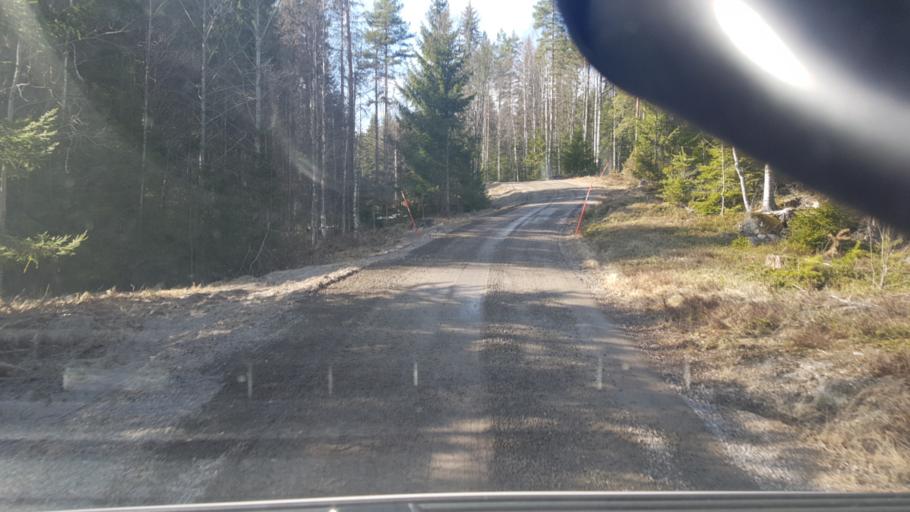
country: SE
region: Vaermland
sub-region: Eda Kommun
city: Amotfors
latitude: 59.8298
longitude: 12.3914
